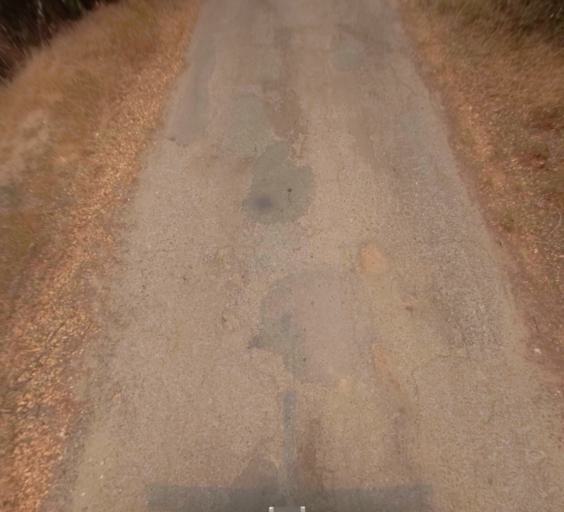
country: US
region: California
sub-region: Fresno County
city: Auberry
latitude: 37.2404
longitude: -119.5065
